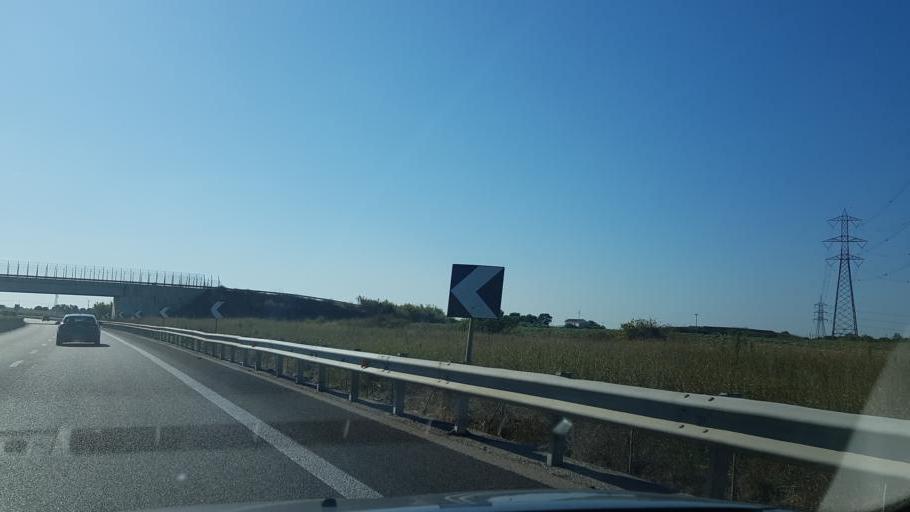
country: IT
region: Apulia
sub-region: Provincia di Brindisi
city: La Rosa
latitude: 40.6008
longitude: 17.9661
